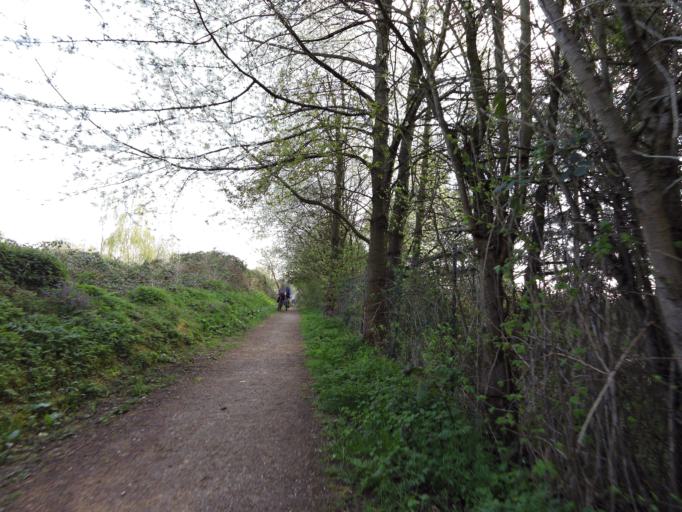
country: DE
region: North Rhine-Westphalia
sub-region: Regierungsbezirk Koln
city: Alfter
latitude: 50.6851
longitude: 7.0151
